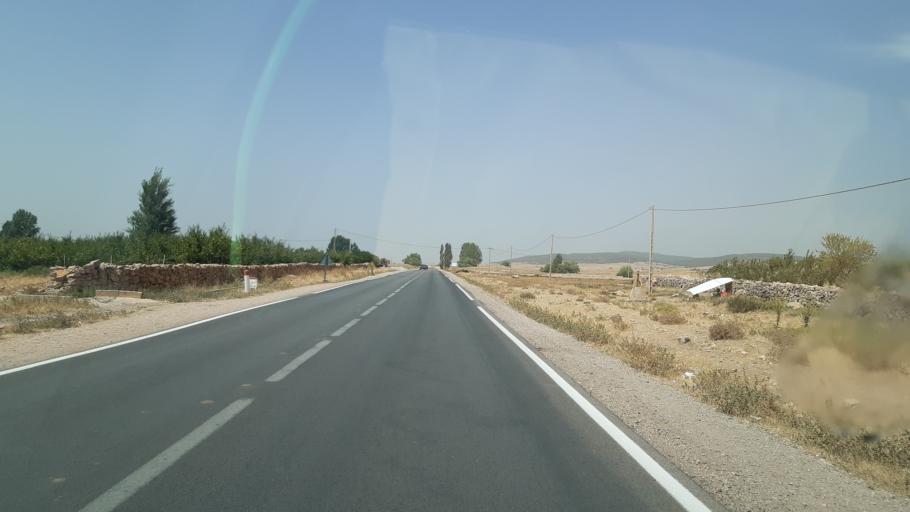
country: MA
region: Meknes-Tafilalet
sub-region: Ifrane
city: Ifrane
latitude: 33.5814
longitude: -5.0908
